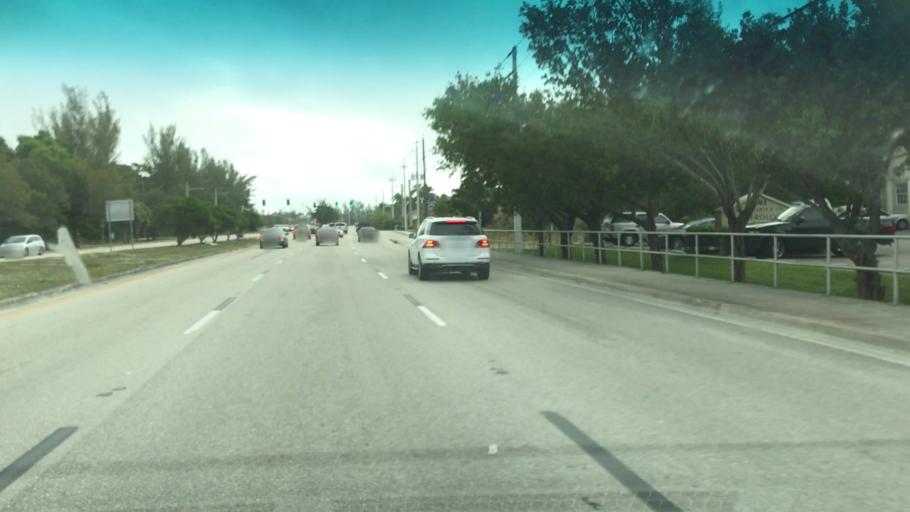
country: US
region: Florida
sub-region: Lee County
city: Cypress Lake
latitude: 26.5206
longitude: -81.8870
